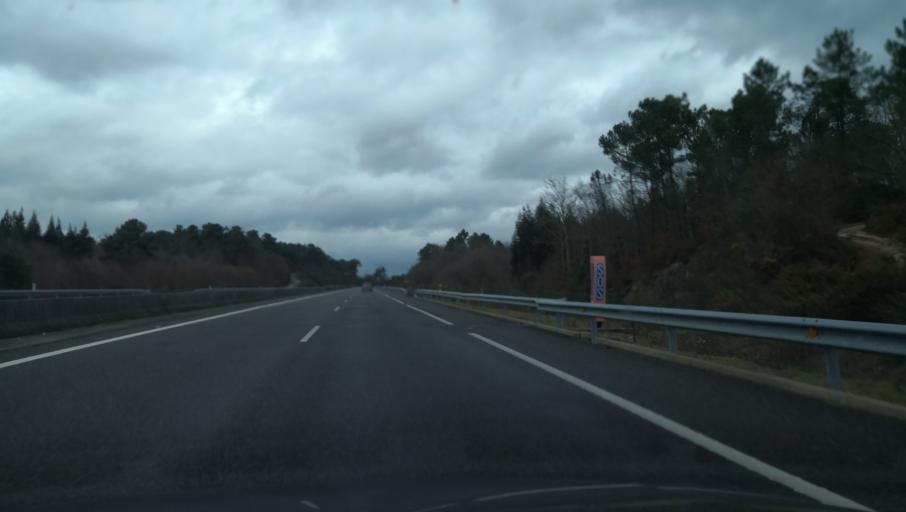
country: ES
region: Galicia
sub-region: Provincia de Ourense
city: Cea
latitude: 42.4702
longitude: -8.0276
